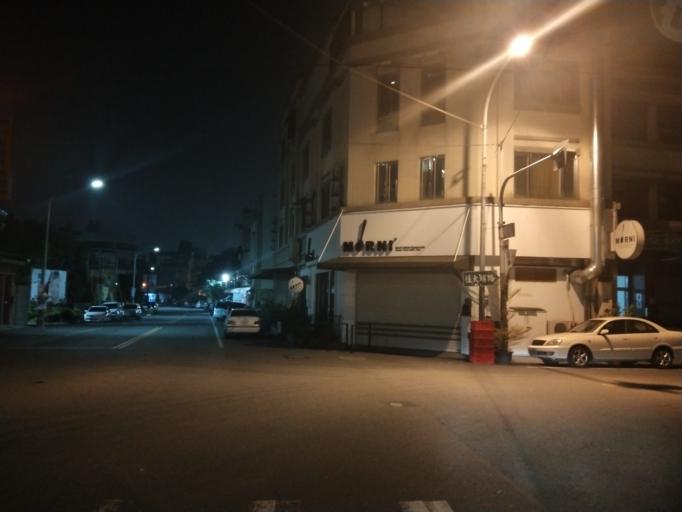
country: TW
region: Taiwan
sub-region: Changhua
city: Chang-hua
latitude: 24.0615
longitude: 120.5437
